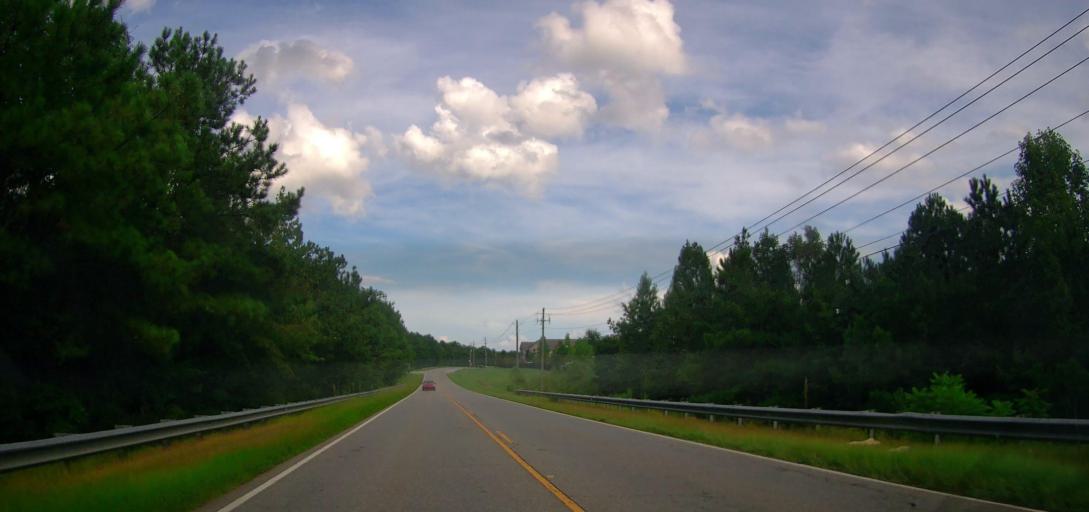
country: US
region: Alabama
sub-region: Russell County
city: Phenix City
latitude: 32.5203
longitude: -85.0251
